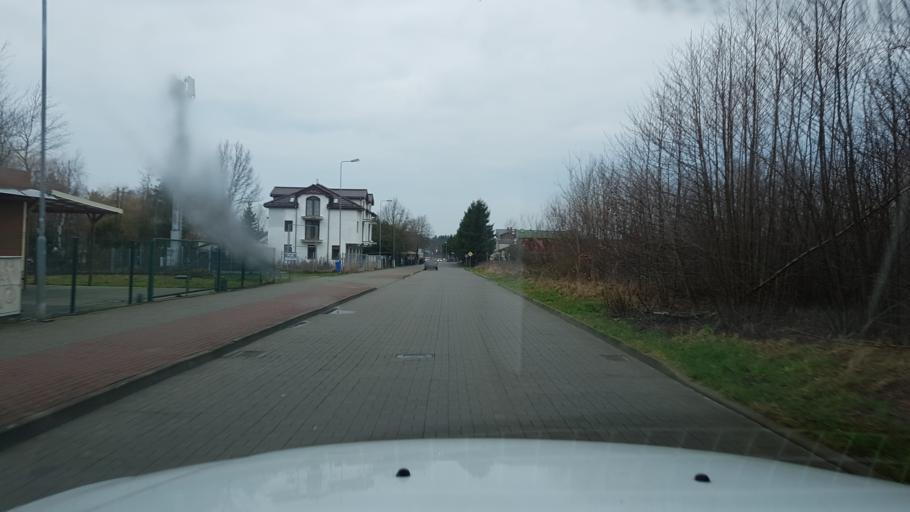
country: PL
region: West Pomeranian Voivodeship
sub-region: Powiat kolobrzeski
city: Grzybowo
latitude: 54.1605
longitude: 15.4930
